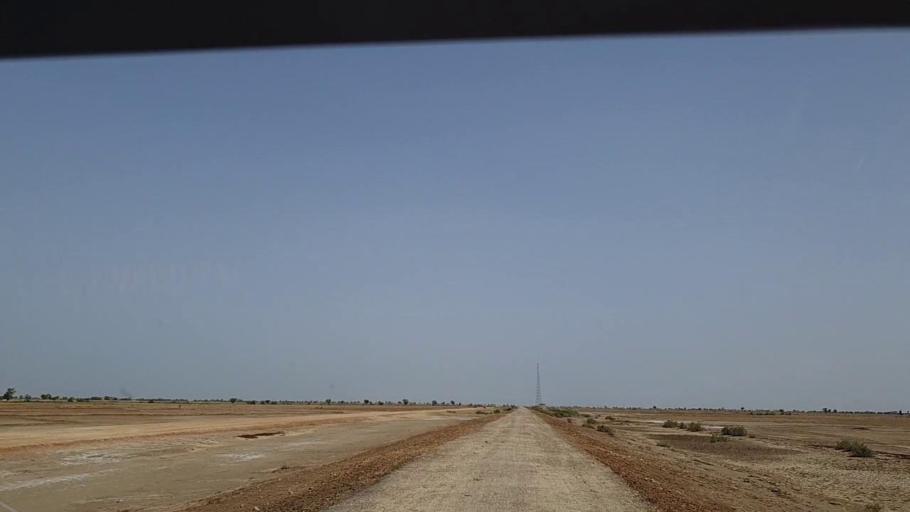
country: PK
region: Sindh
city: Phulji
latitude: 26.7983
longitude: 67.6372
